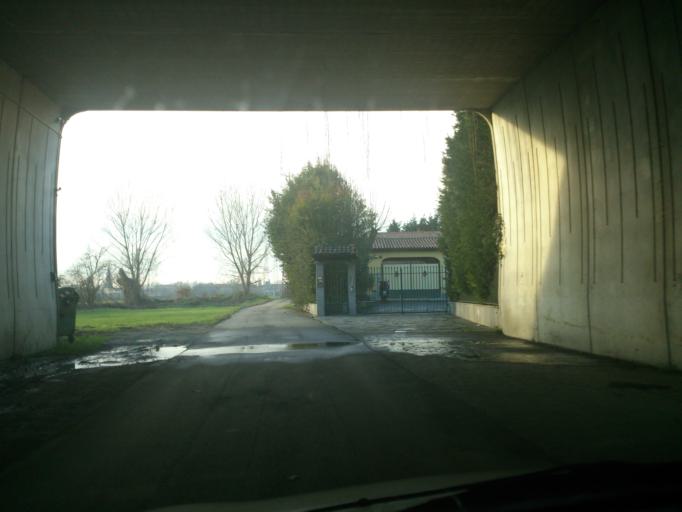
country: IT
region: Lombardy
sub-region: Citta metropolitana di Milano
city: Chiaravalle
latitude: 45.4142
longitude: 9.2518
